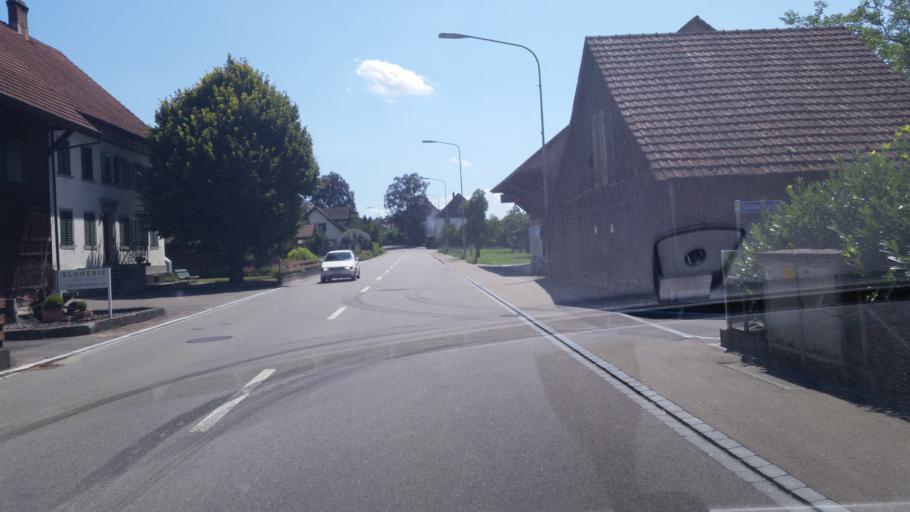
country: CH
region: Zurich
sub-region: Bezirk Buelach
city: Glattfelden
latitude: 47.5582
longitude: 8.5038
